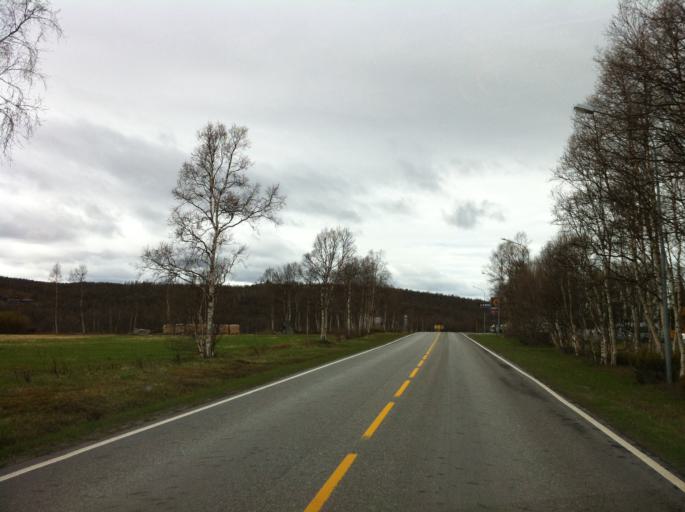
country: NO
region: Sor-Trondelag
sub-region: Tydal
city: Aas
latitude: 62.6464
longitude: 11.8762
